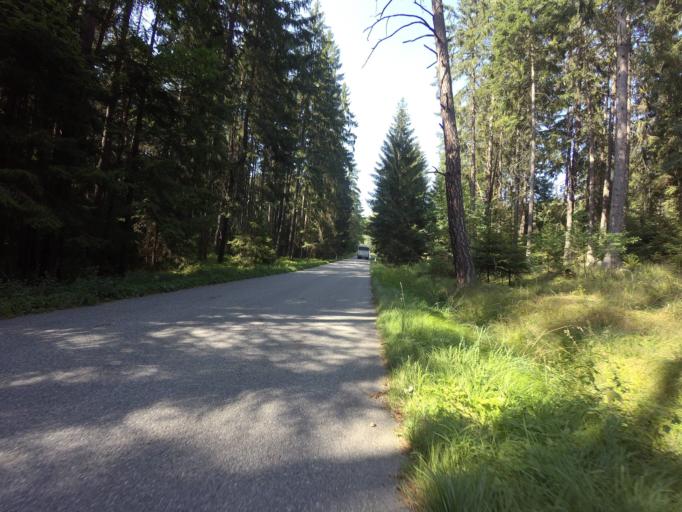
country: CZ
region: Jihocesky
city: Tyn nad Vltavou
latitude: 49.1593
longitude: 14.4298
